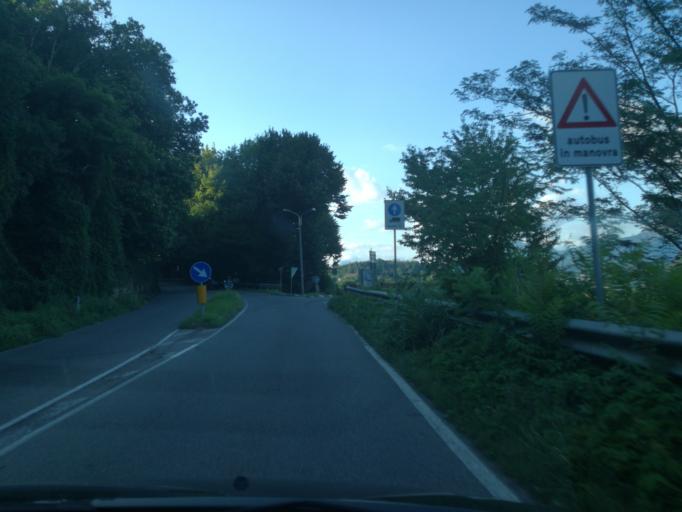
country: IT
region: Lombardy
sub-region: Provincia di Lecco
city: Imbersago
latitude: 45.7009
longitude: 9.4446
